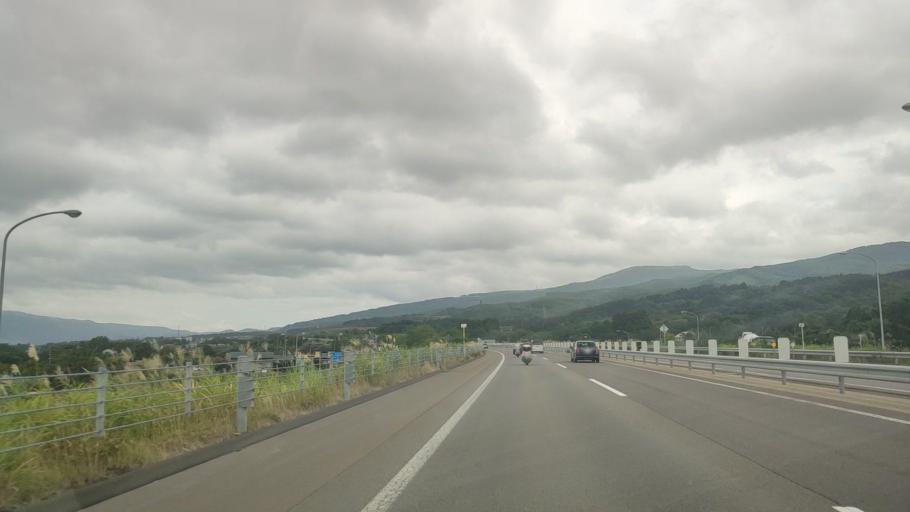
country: JP
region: Hokkaido
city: Nanae
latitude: 41.8673
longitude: 140.7300
